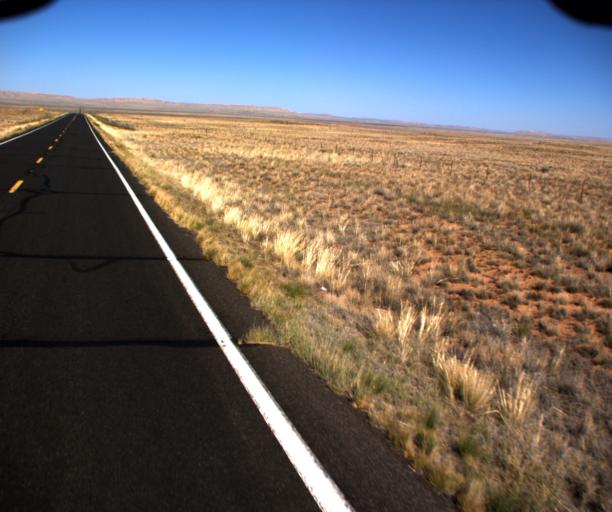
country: US
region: Arizona
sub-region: Navajo County
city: First Mesa
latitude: 35.6581
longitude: -110.4920
